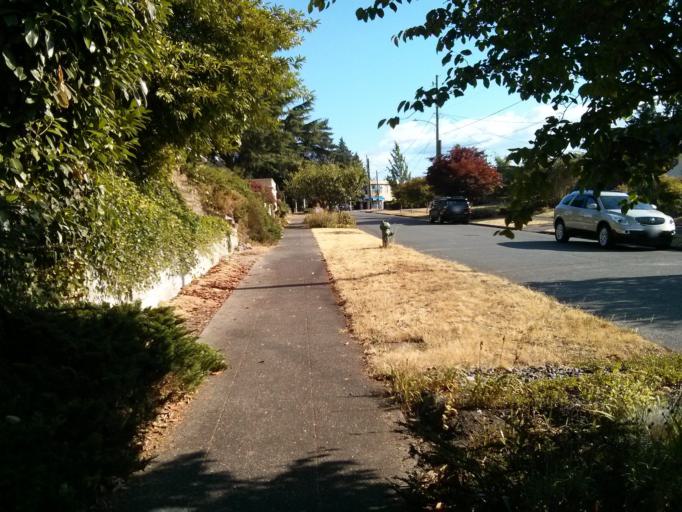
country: US
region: Washington
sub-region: King County
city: Seattle
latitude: 47.5823
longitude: -122.3918
